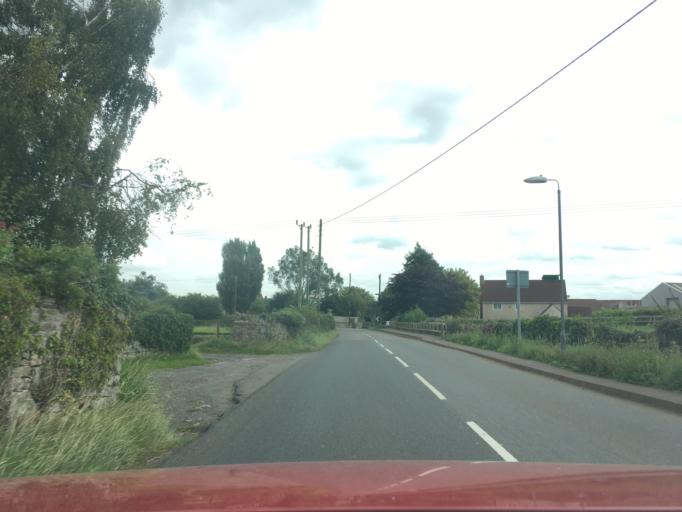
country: GB
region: England
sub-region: South Gloucestershire
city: Tytherington
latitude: 51.5912
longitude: -2.4757
